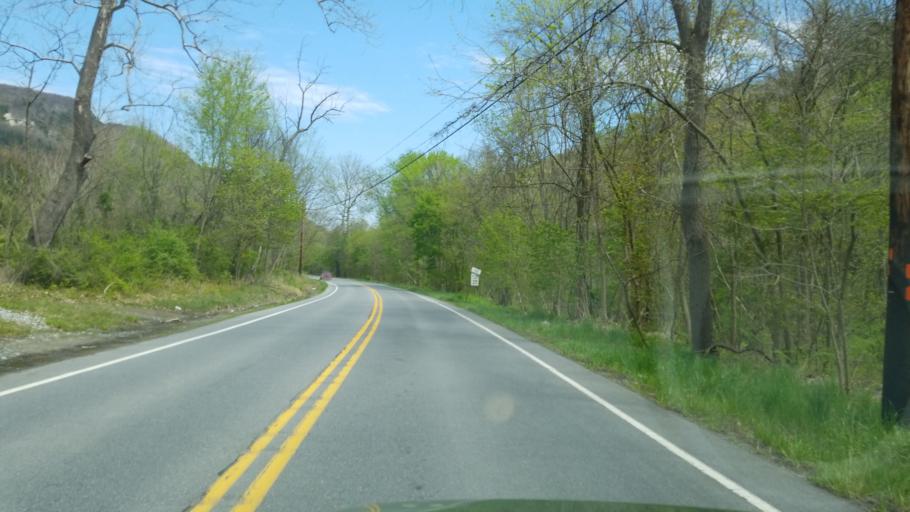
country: US
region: Pennsylvania
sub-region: Huntingdon County
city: Mount Union
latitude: 40.3940
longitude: -77.9350
